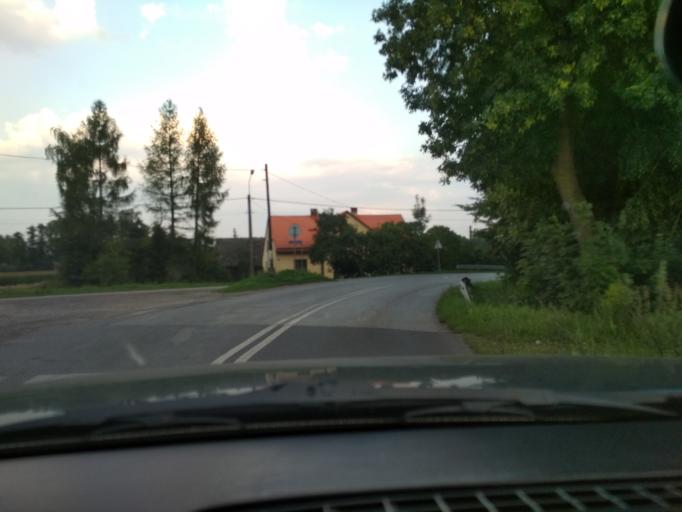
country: PL
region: Silesian Voivodeship
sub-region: Powiat cieszynski
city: Strumien
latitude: 49.9127
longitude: 18.7680
